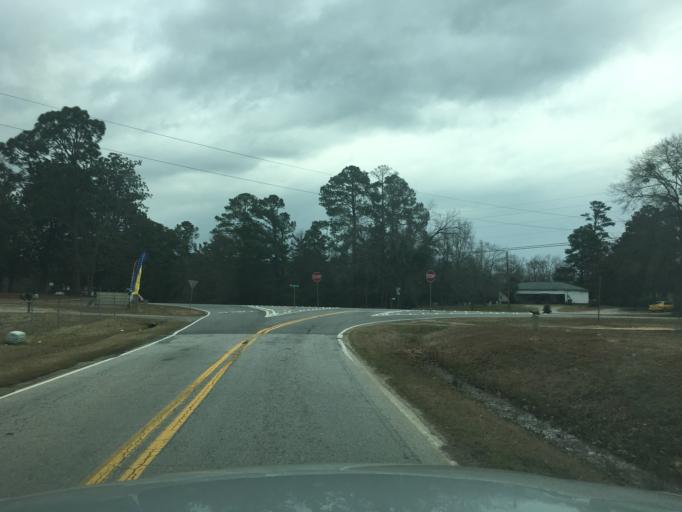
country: US
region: Georgia
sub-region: Columbia County
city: Appling
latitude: 33.6627
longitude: -82.3357
